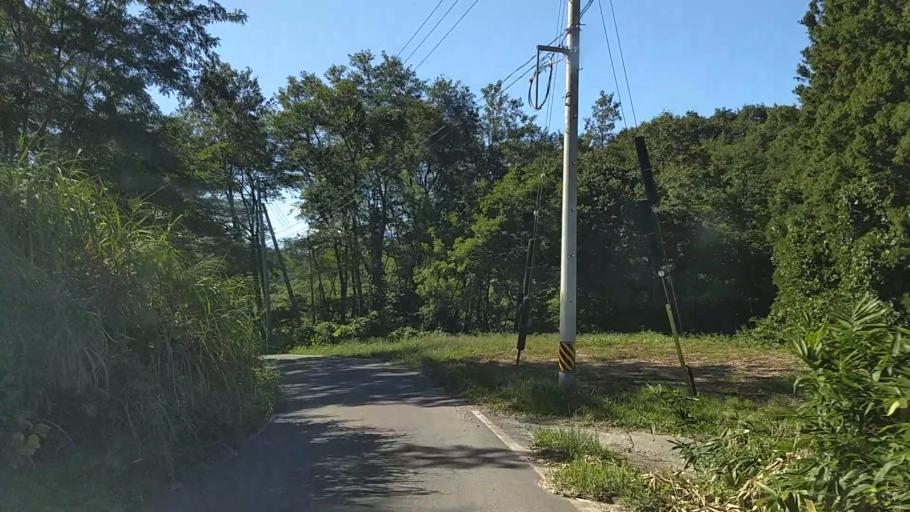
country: JP
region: Nagano
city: Nagano-shi
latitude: 36.5883
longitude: 138.0886
